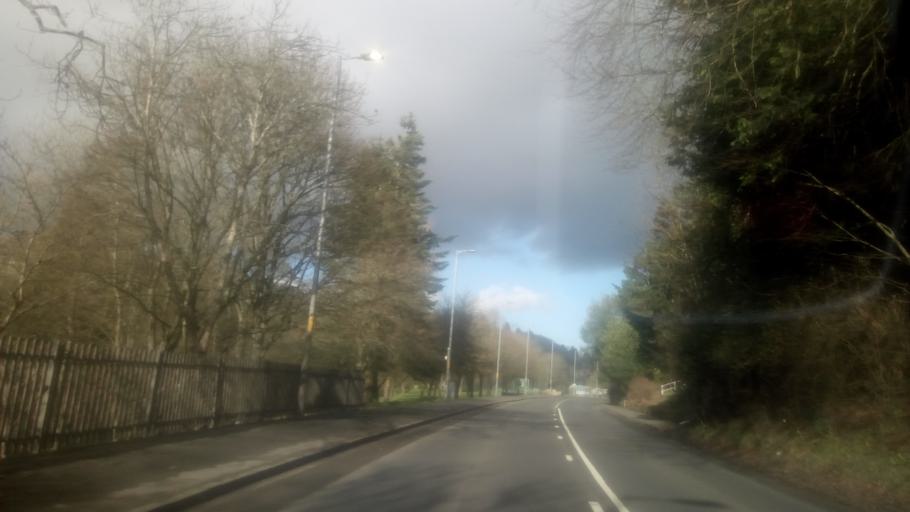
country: GB
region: Scotland
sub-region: The Scottish Borders
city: Hawick
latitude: 55.4189
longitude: -2.8044
